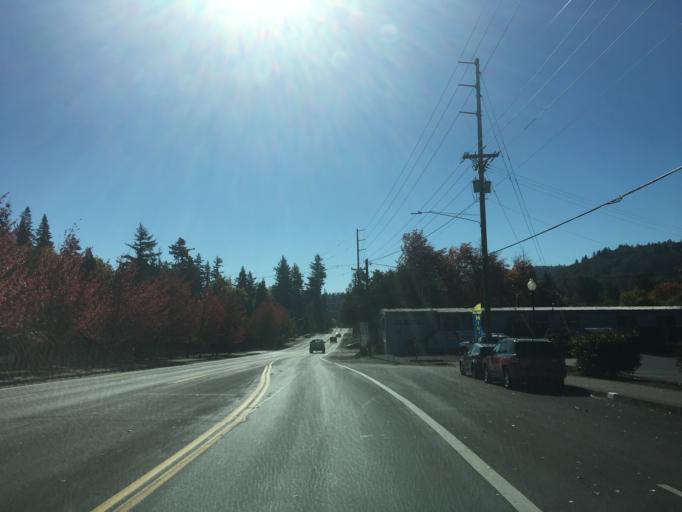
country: US
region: Oregon
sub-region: Multnomah County
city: Gresham
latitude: 45.4866
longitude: -122.4139
